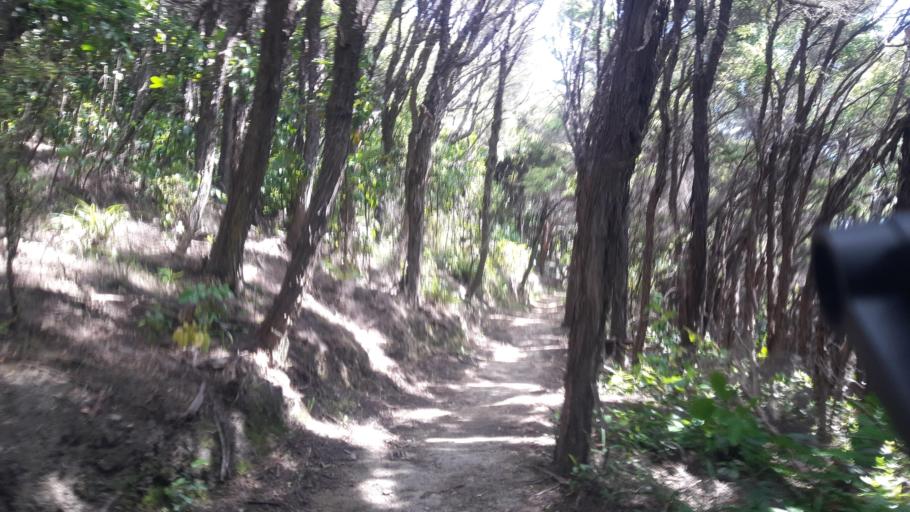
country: NZ
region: Marlborough
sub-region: Marlborough District
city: Picton
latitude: -41.2545
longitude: 174.0416
